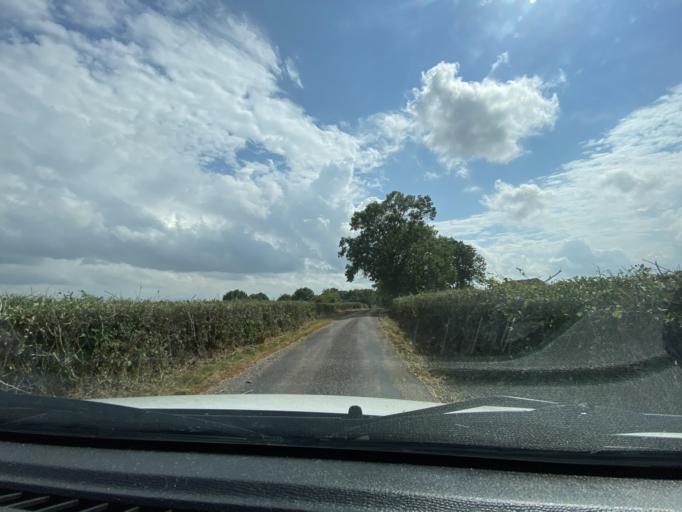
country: FR
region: Bourgogne
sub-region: Departement de la Cote-d'Or
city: Saulieu
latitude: 47.2962
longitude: 4.2355
